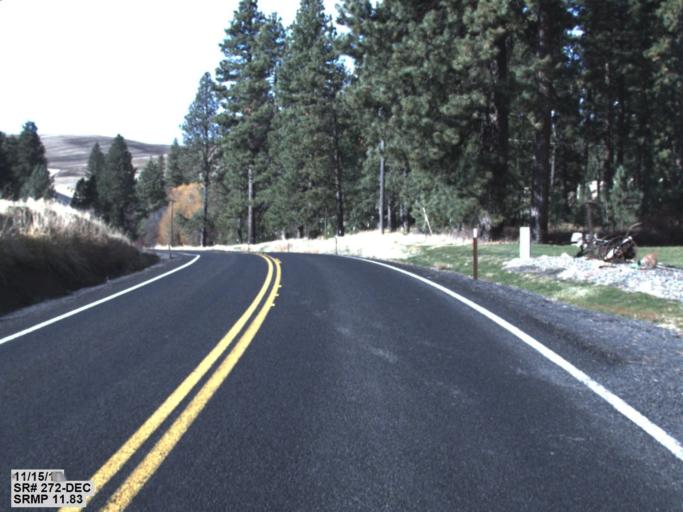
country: US
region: Washington
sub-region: Whitman County
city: Pullman
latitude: 46.9402
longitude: -117.1506
